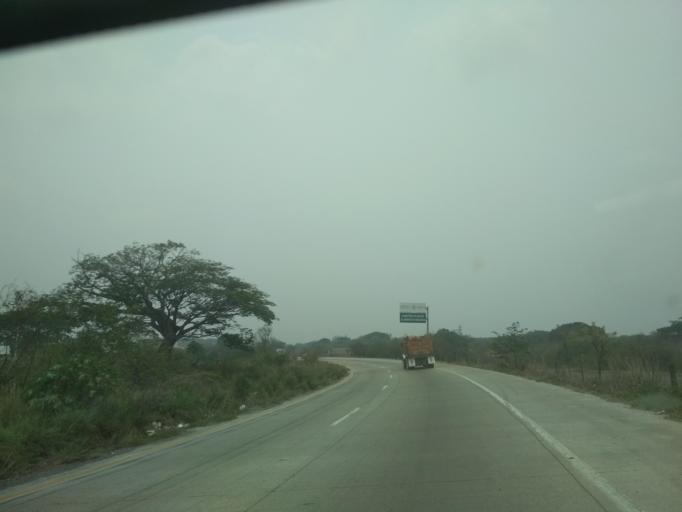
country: MX
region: Veracruz
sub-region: Veracruz
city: Oasis
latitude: 19.1911
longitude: -96.2455
